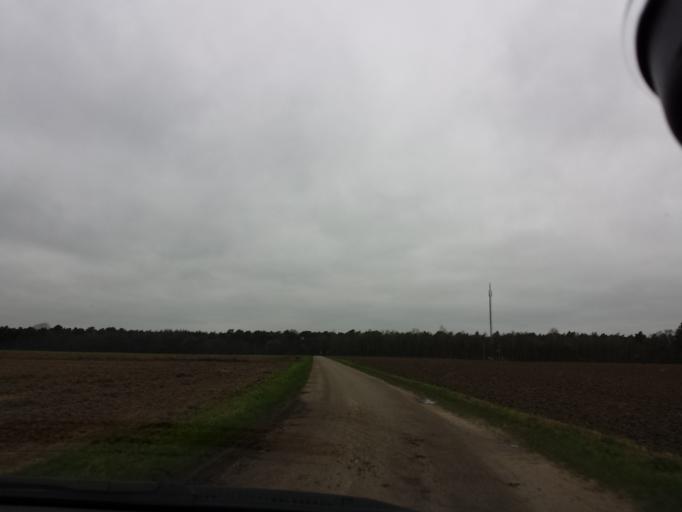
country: DE
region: North Rhine-Westphalia
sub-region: Regierungsbezirk Koln
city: Waldfeucht
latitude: 51.0952
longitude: 6.0035
